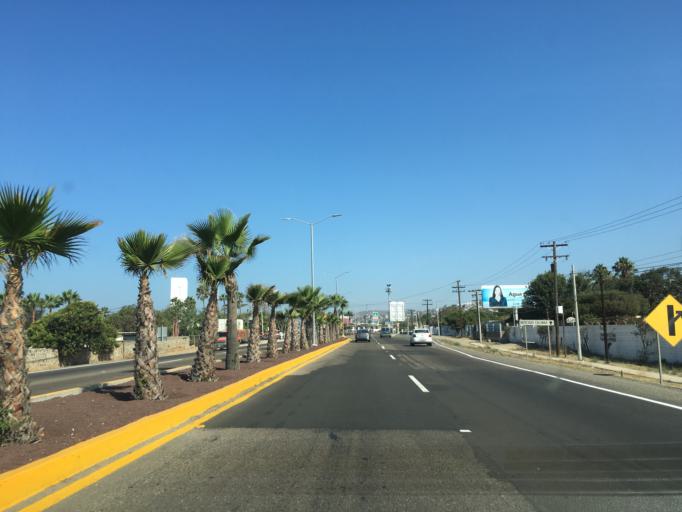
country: MX
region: Baja California
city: El Sauzal
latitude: 31.8833
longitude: -116.6851
